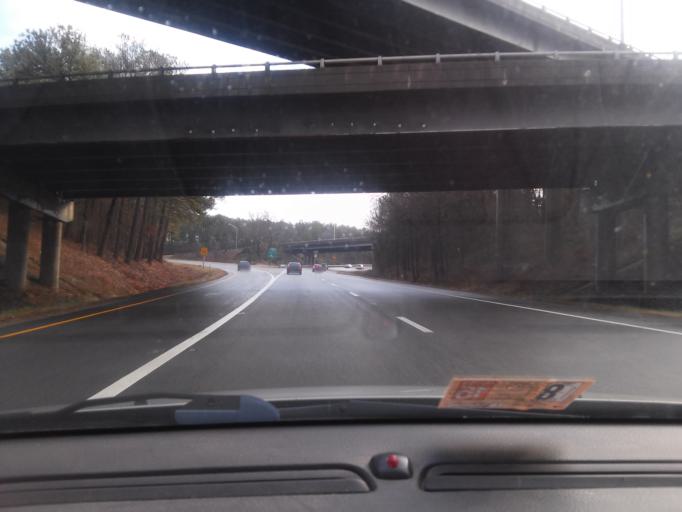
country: US
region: Virginia
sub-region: Henrico County
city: Lakeside
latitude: 37.5867
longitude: -77.4750
